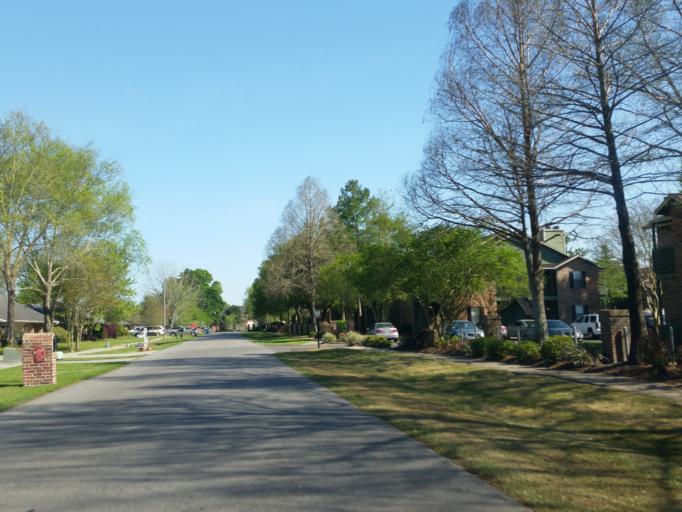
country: US
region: Louisiana
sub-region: Lafayette Parish
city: Milton
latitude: 30.1493
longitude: -92.0525
